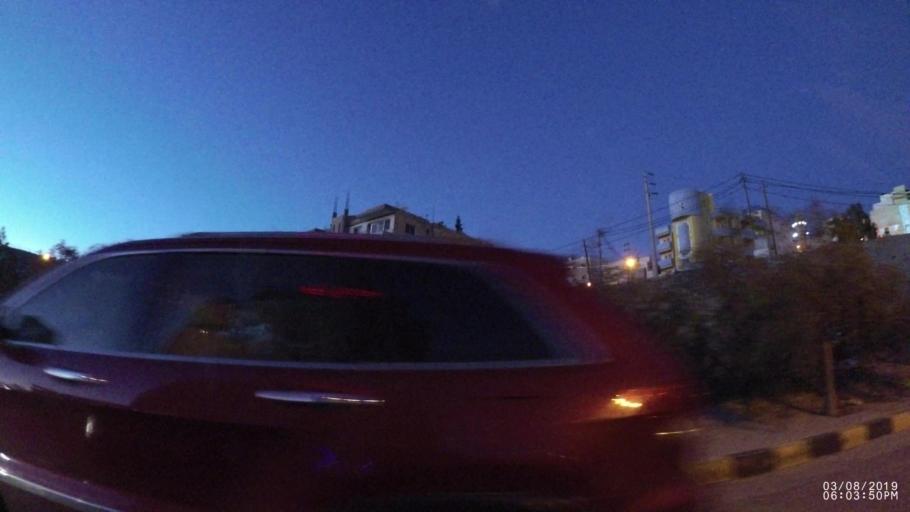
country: JO
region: Ma'an
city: Petra
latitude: 30.3263
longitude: 35.4705
